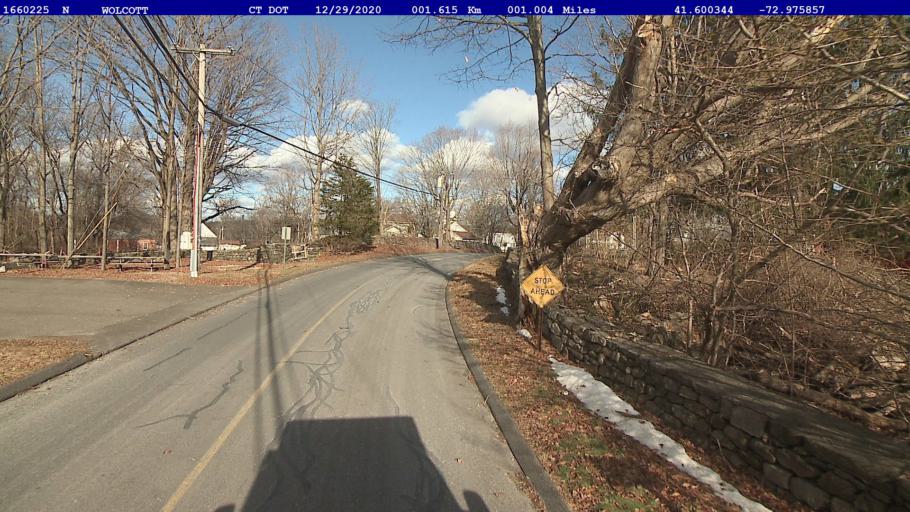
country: US
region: Connecticut
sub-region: New Haven County
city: Wolcott
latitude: 41.6003
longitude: -72.9758
